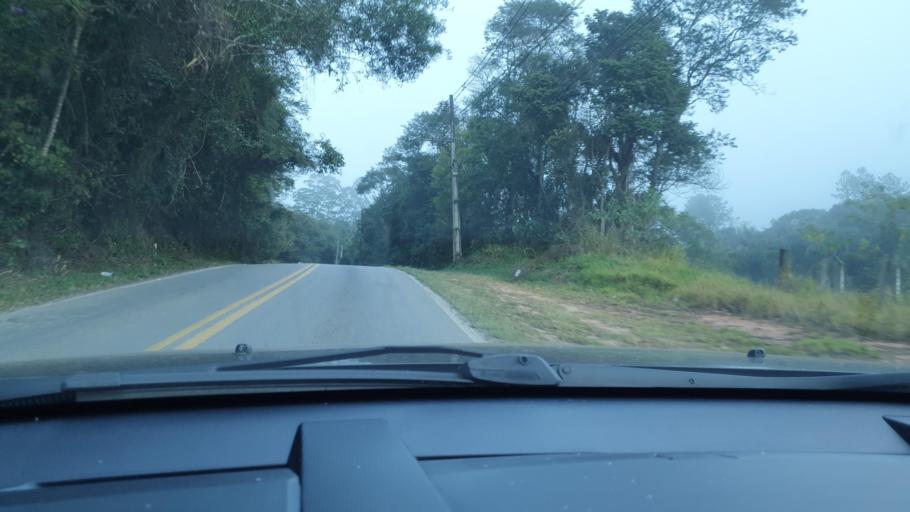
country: BR
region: Sao Paulo
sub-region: Ibiuna
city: Ibiuna
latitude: -23.6836
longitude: -47.2598
